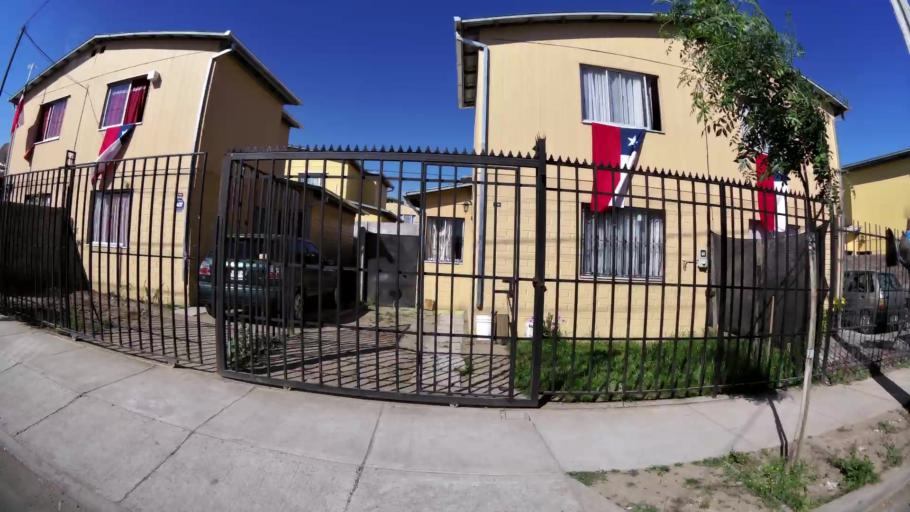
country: CL
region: Santiago Metropolitan
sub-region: Provincia de Santiago
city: La Pintana
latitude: -33.6195
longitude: -70.6203
